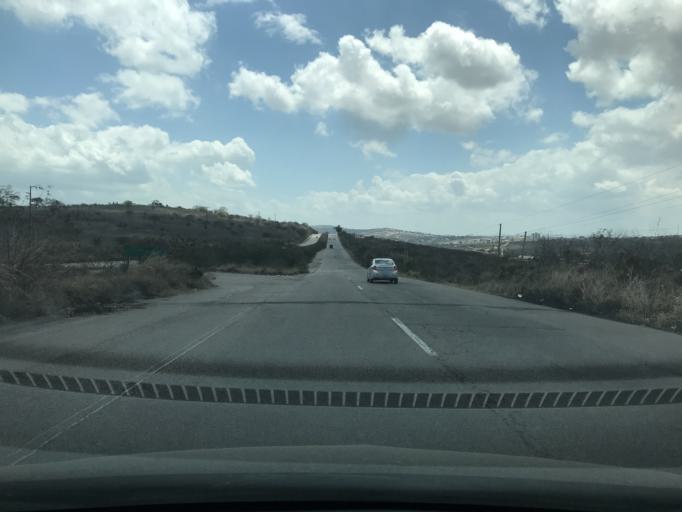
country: BR
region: Pernambuco
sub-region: Caruaru
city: Caruaru
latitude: -8.3052
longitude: -35.9327
